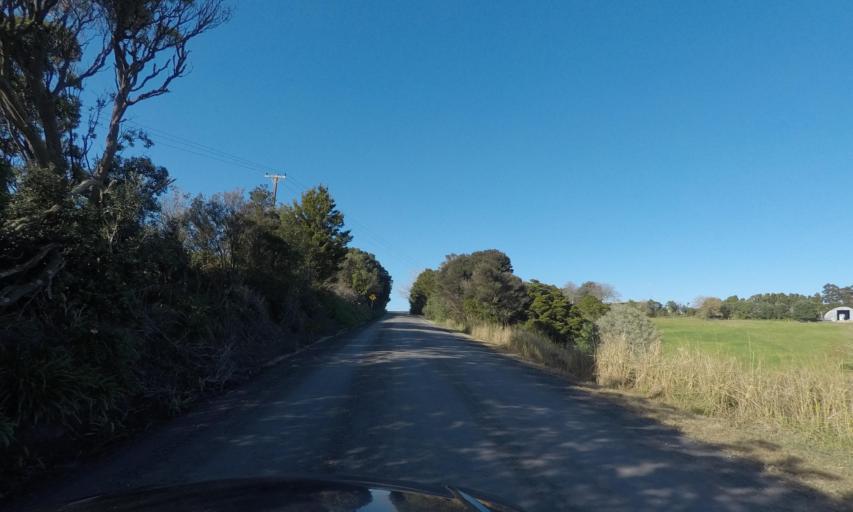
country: NZ
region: Auckland
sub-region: Auckland
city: Wellsford
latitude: -36.1602
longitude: 174.6030
